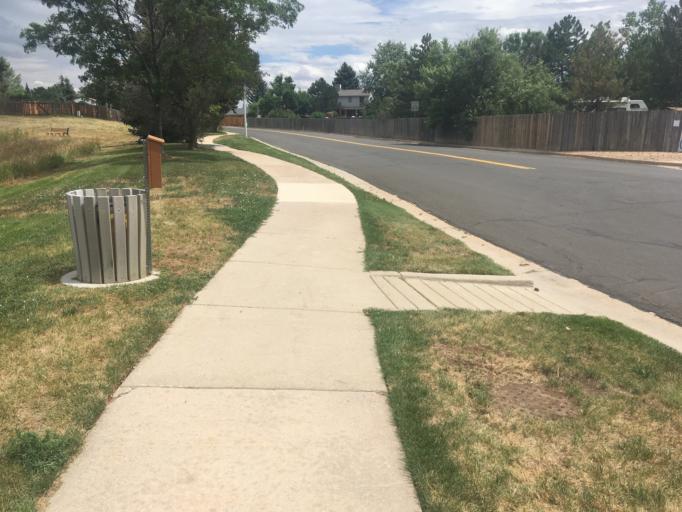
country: US
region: Colorado
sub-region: Broomfield County
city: Broomfield
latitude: 39.9305
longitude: -105.1036
